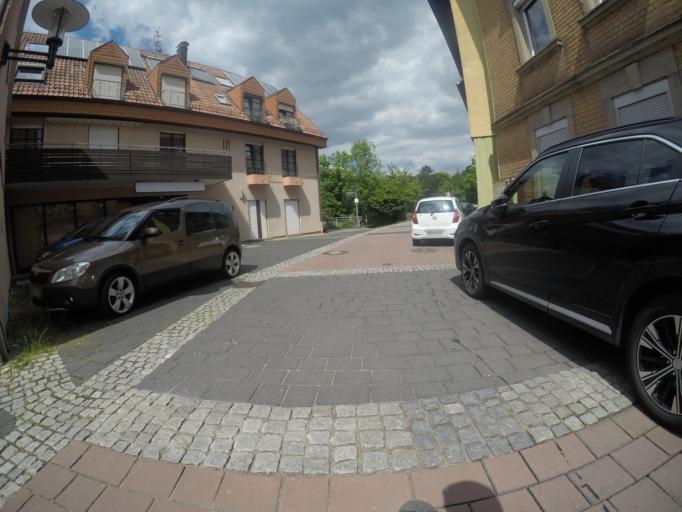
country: DE
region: Baden-Wuerttemberg
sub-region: Karlsruhe Region
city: Pforzheim
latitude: 48.8690
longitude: 8.6833
